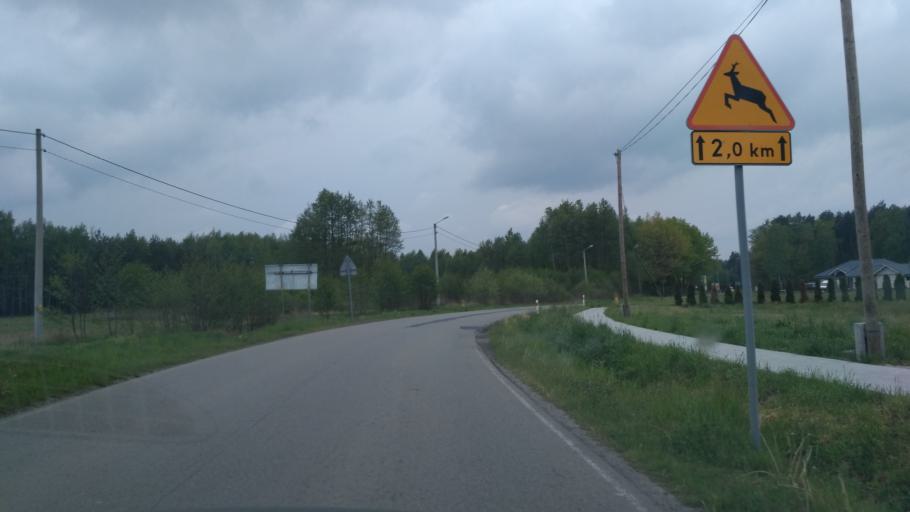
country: PL
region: Subcarpathian Voivodeship
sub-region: Powiat kolbuszowski
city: Kolbuszowa
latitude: 50.1992
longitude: 21.7739
